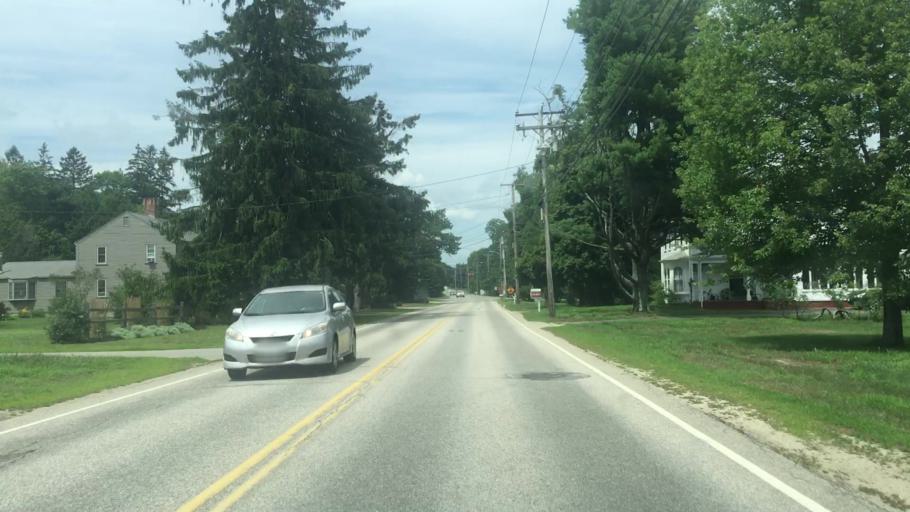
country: US
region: Maine
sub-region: Cumberland County
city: Scarborough
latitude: 43.5893
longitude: -70.2950
